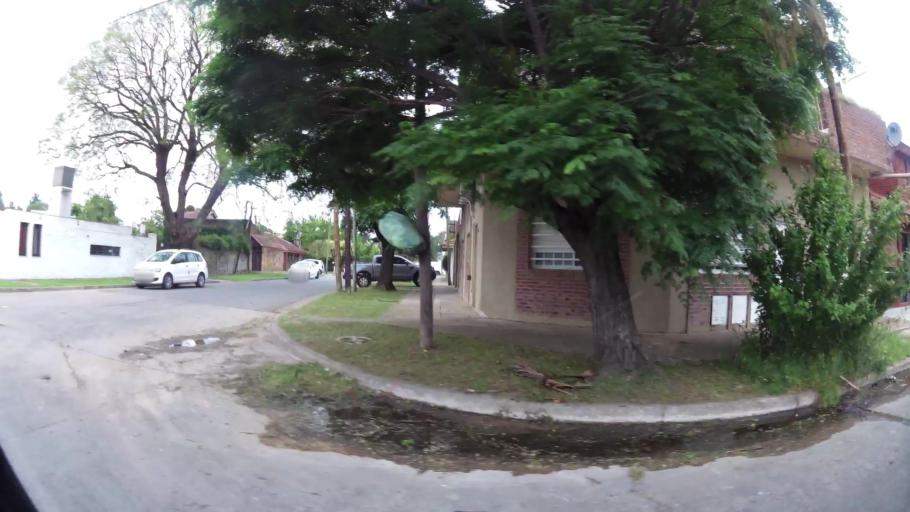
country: AR
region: Buenos Aires
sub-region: Partido de La Plata
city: La Plata
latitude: -34.9379
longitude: -57.9870
